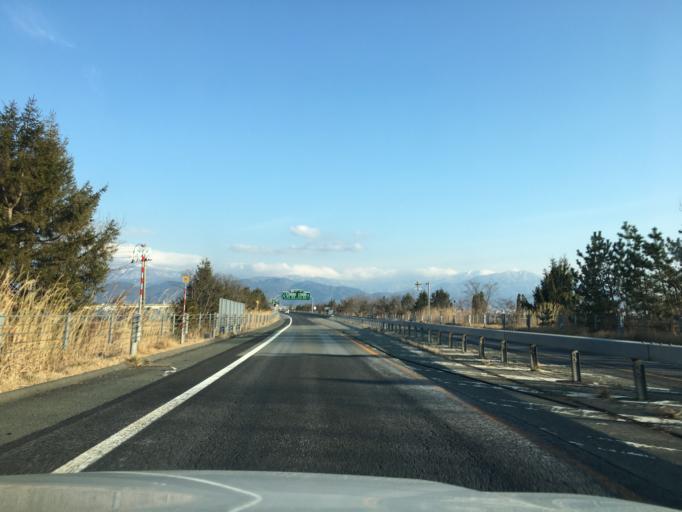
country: JP
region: Yamagata
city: Sagae
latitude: 38.3169
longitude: 140.3059
